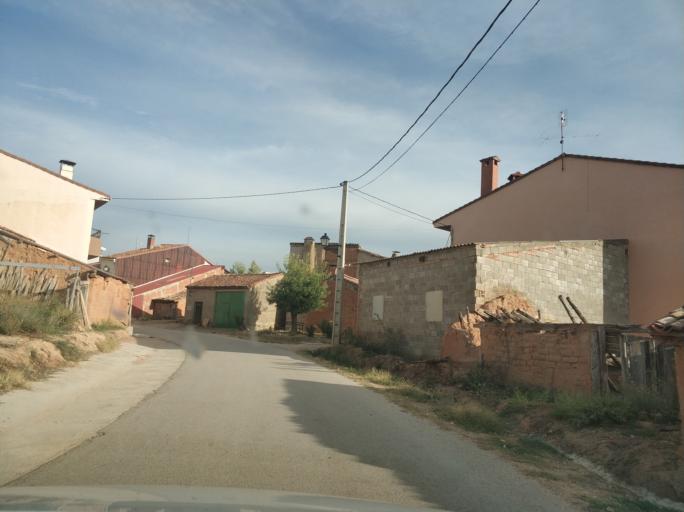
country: ES
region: Castille and Leon
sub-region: Provincia de Soria
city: Fuentearmegil
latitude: 41.6610
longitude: -3.2173
